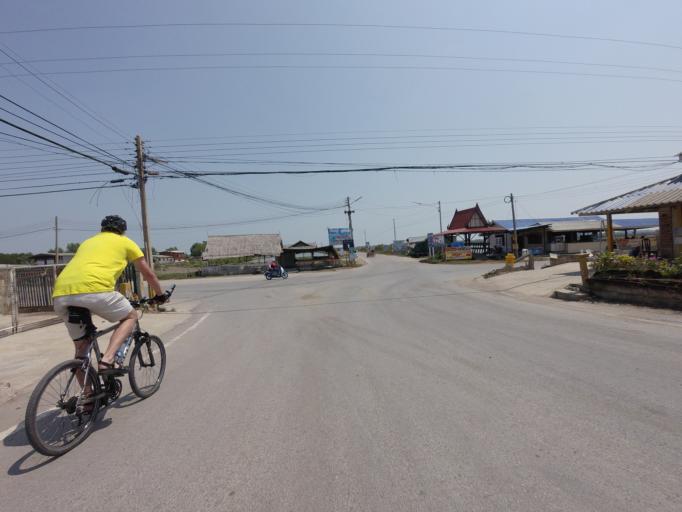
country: TH
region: Samut Sakhon
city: Samut Sakhon
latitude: 13.5133
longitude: 100.3856
